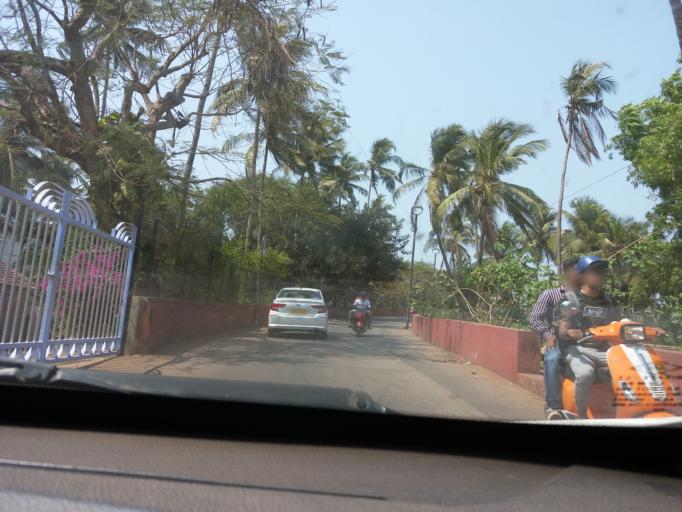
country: IN
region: Goa
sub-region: North Goa
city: Taleigao
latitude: 15.4528
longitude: 73.8023
